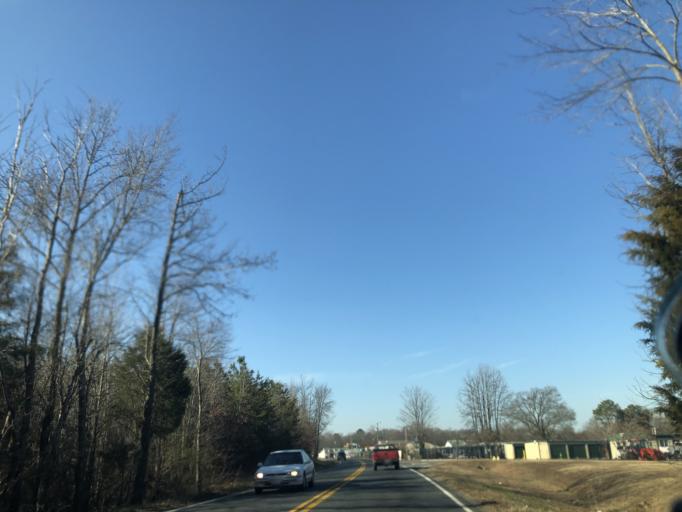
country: US
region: Virginia
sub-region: Spotsylvania County
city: Spotsylvania Courthouse
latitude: 38.1327
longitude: -77.5177
